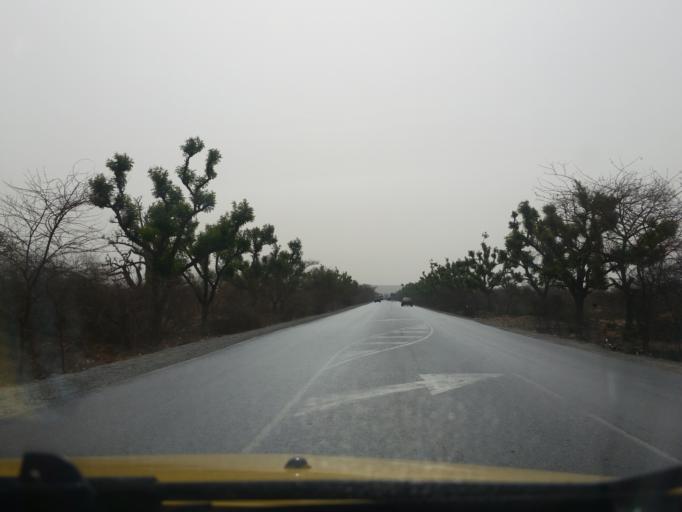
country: SN
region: Thies
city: Pout
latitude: 14.7633
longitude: -17.0225
